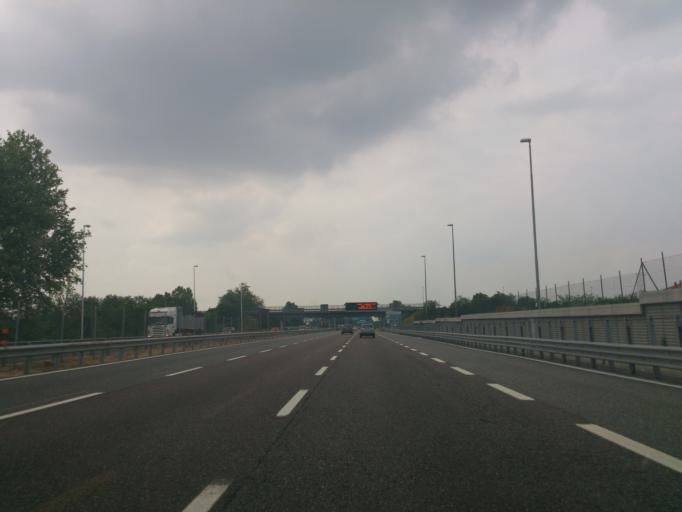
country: IT
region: Lombardy
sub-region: Citta metropolitana di Milano
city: Carugate
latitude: 45.5567
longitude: 9.3303
